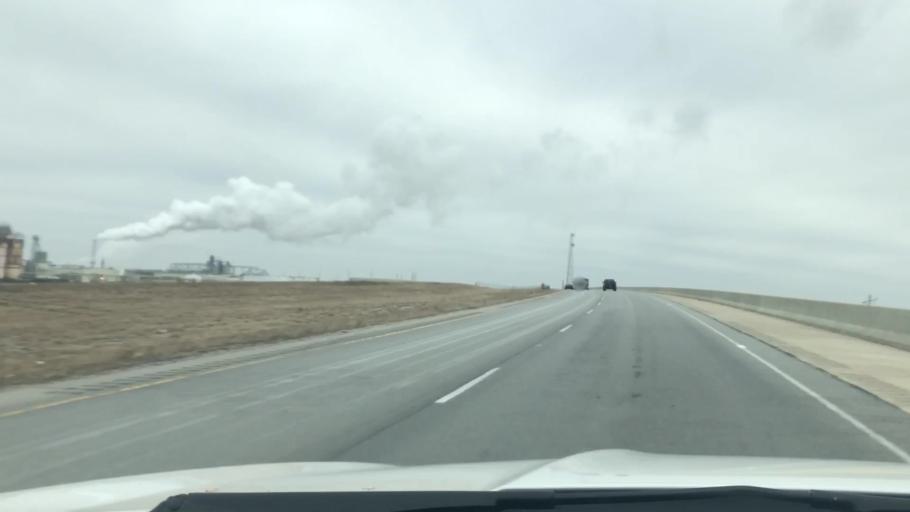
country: US
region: Indiana
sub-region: Cass County
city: Dunkirk
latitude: 40.7114
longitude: -86.4421
